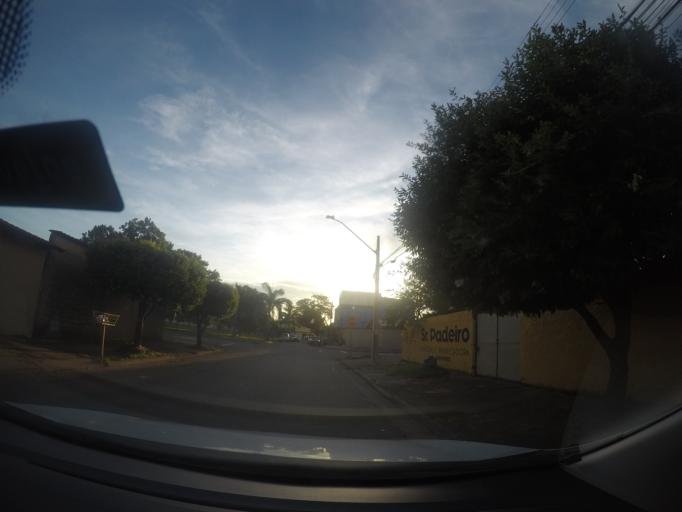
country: BR
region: Goias
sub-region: Goiania
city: Goiania
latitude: -16.6876
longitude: -49.3178
